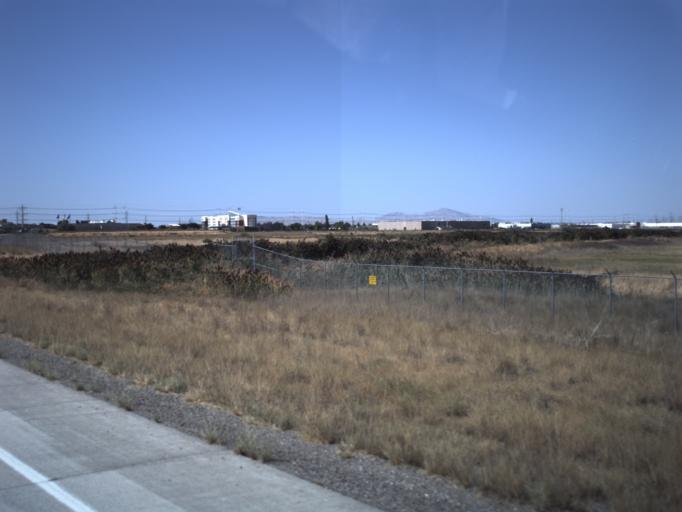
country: US
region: Utah
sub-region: Salt Lake County
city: West Valley City
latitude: 40.7660
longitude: -111.9928
